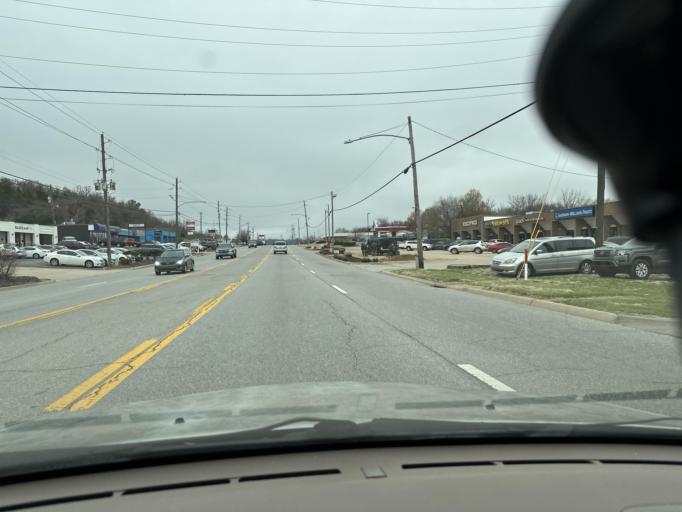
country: US
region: Arkansas
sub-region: Washington County
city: Johnson
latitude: 36.1037
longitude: -94.1479
